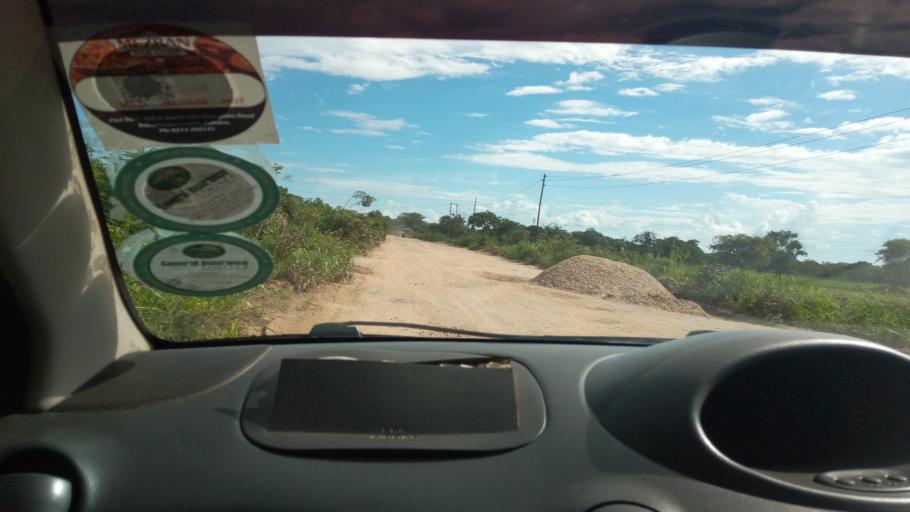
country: ZM
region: Lusaka
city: Lusaka
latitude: -15.5270
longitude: 28.3420
